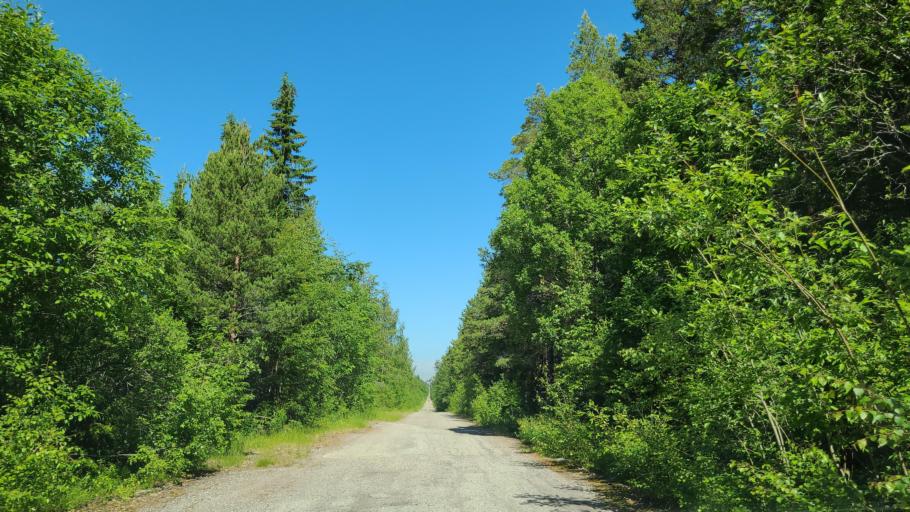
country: SE
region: Vaesternorrland
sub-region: OErnskoeldsviks Kommun
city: Husum
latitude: 63.4179
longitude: 19.2217
